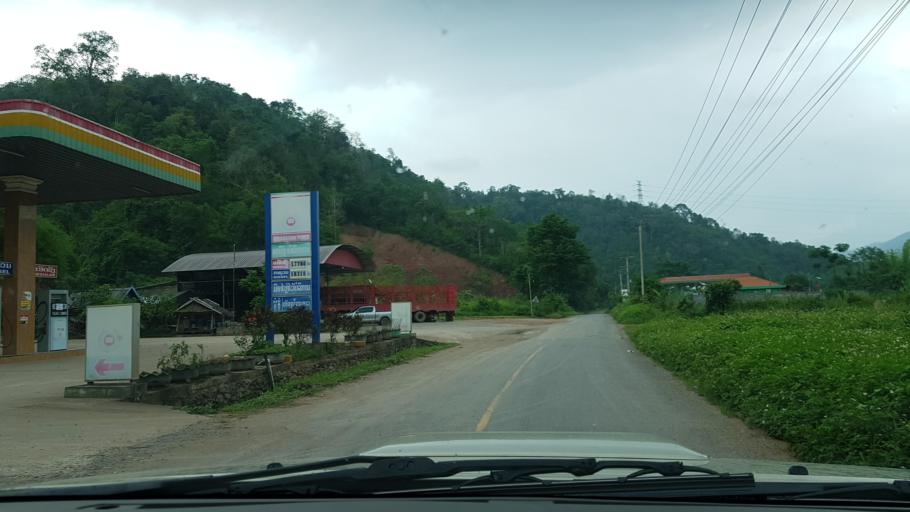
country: LA
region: Oudomxai
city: Muang Xay
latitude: 20.6271
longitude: 101.9612
